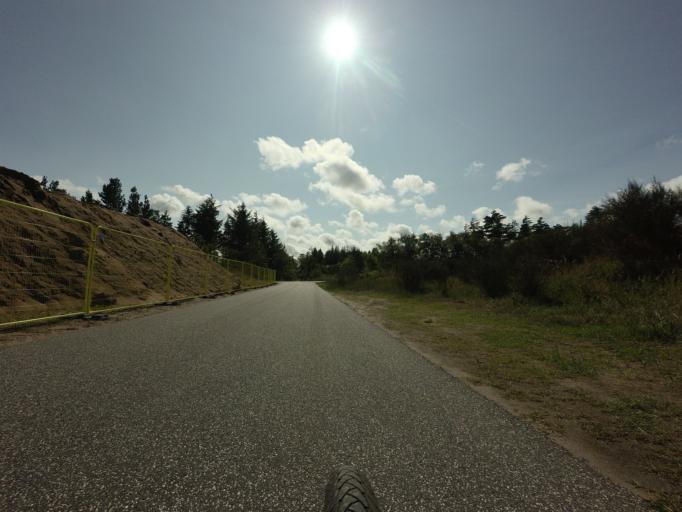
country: DK
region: North Denmark
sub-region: Hjorring Kommune
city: Hirtshals
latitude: 57.5840
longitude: 9.9889
